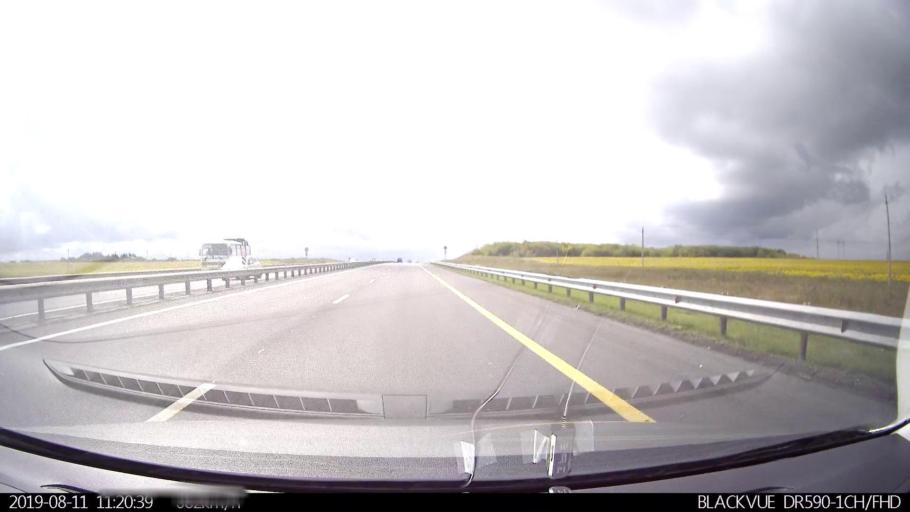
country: RU
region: Ulyanovsk
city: Novoul'yanovsk
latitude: 54.1554
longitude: 48.2644
